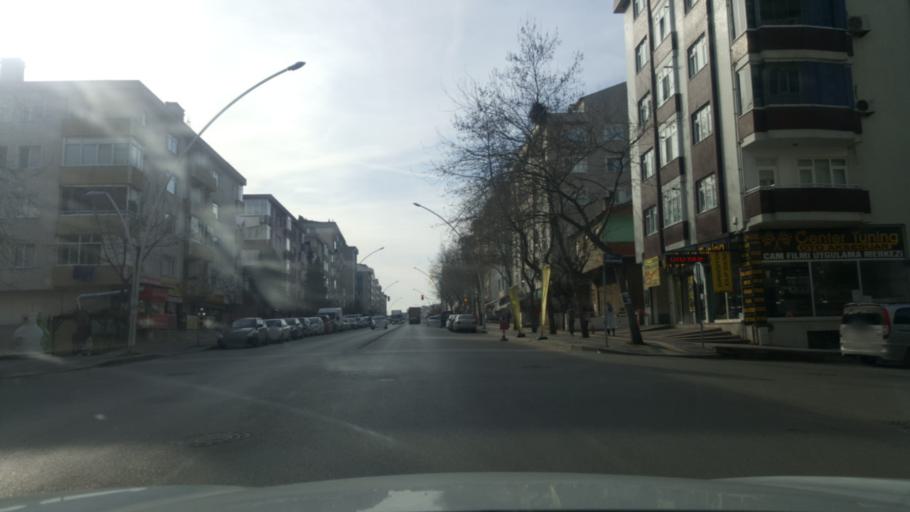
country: TR
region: Kocaeli
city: Gebze
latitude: 40.7917
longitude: 29.4378
